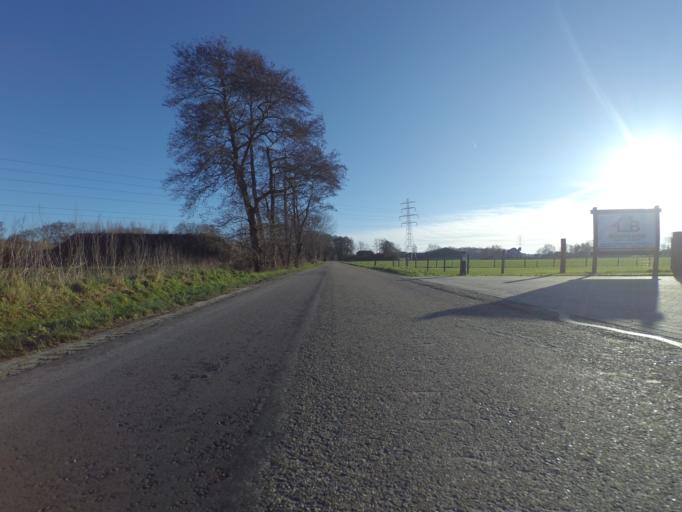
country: NL
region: Gelderland
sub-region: Gemeente Putten
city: Putten
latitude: 52.2513
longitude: 5.5742
